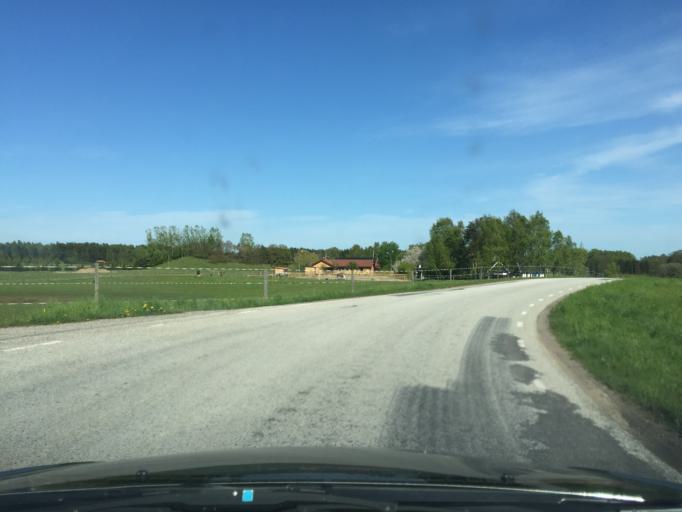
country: SE
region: Skane
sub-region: Sjobo Kommun
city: Blentarp
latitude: 55.5734
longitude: 13.5761
